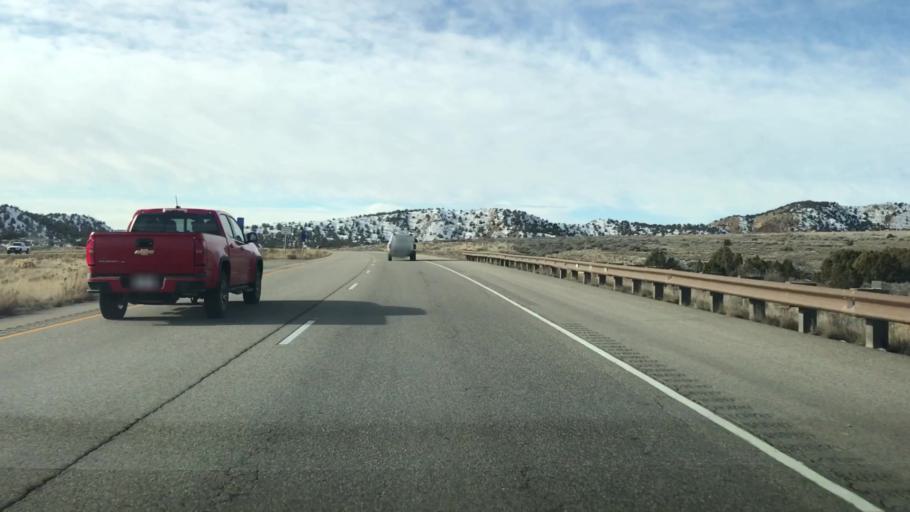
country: US
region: Colorado
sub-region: Garfield County
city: Parachute
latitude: 39.3849
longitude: -108.1491
